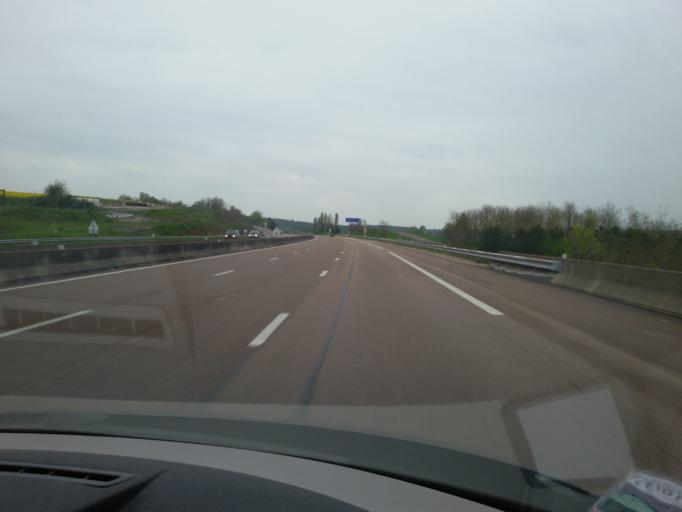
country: FR
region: Bourgogne
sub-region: Departement de la Cote-d'Or
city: Selongey
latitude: 47.5804
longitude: 5.2105
